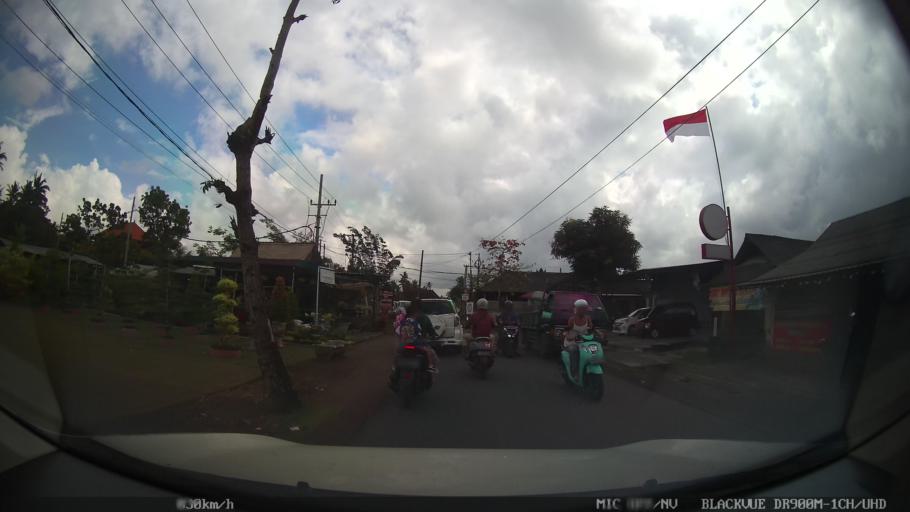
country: ID
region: Bali
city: Banjar Bucu
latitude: -8.5788
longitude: 115.2045
